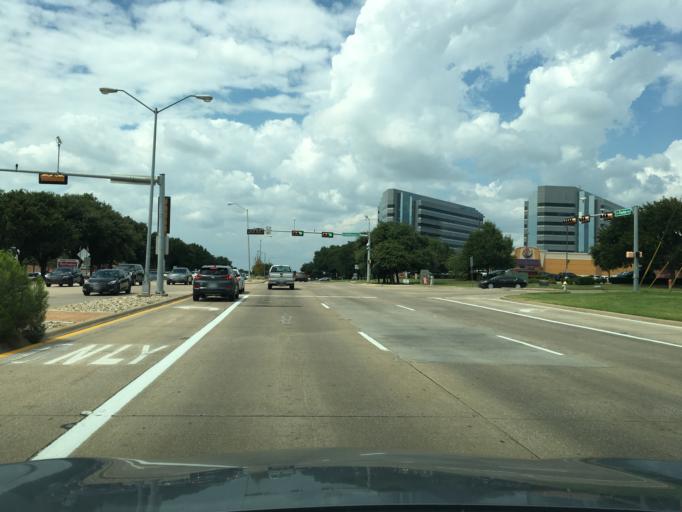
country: US
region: Texas
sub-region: Dallas County
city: Addison
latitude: 33.0211
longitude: -96.7951
